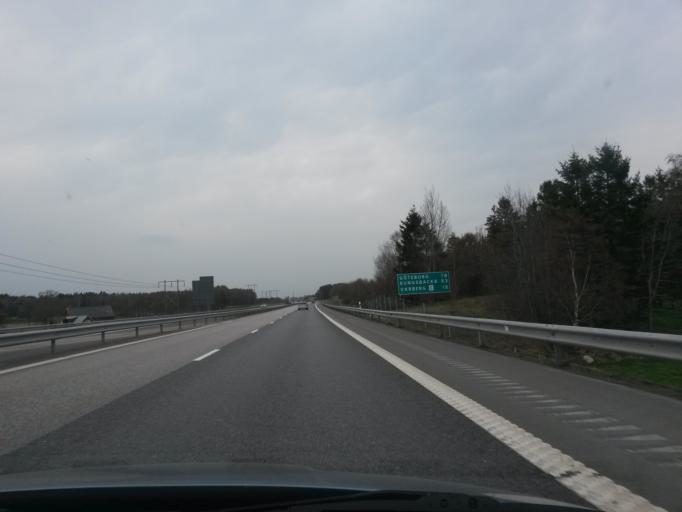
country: SE
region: Halland
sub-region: Varbergs Kommun
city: Tvaaker
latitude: 57.0765
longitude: 12.3509
